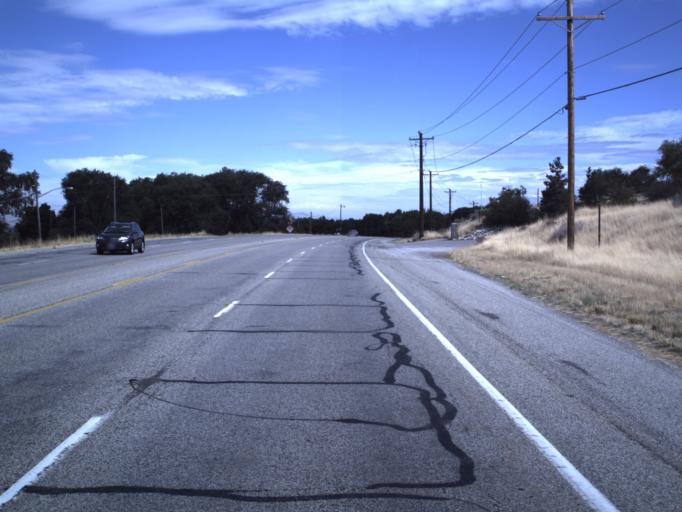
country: US
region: Utah
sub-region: Box Elder County
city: Willard
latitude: 41.3896
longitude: -112.0337
